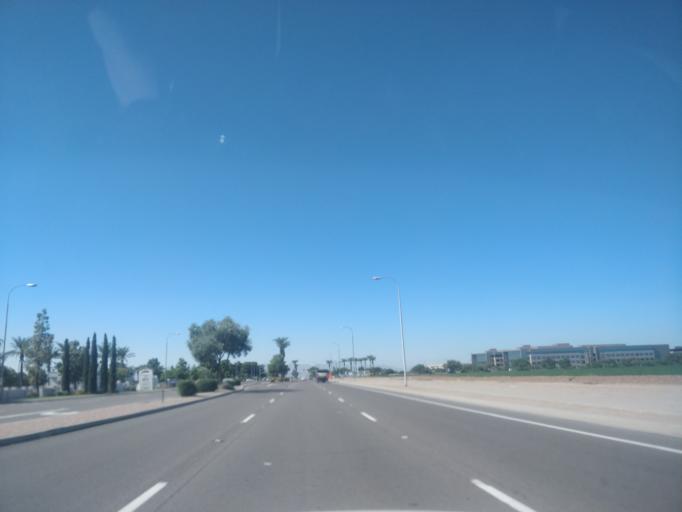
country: US
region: Arizona
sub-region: Maricopa County
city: Sun Lakes
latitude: 33.2616
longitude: -111.8850
